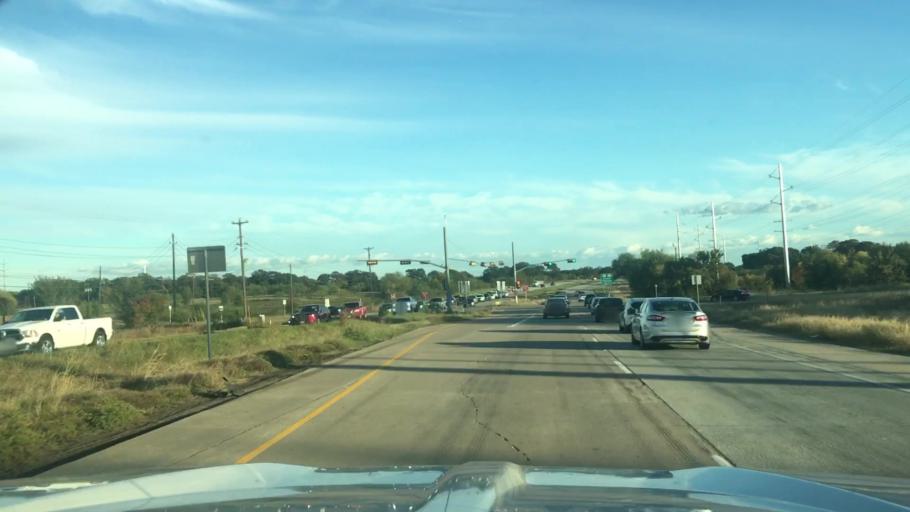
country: US
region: Texas
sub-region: Denton County
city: Denton
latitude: 33.2490
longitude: -97.0959
